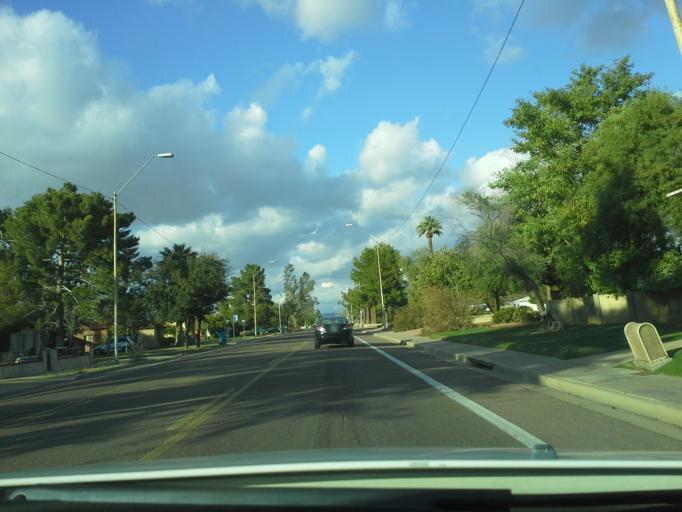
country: US
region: Arizona
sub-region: Maricopa County
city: Phoenix
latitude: 33.4683
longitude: -112.0914
